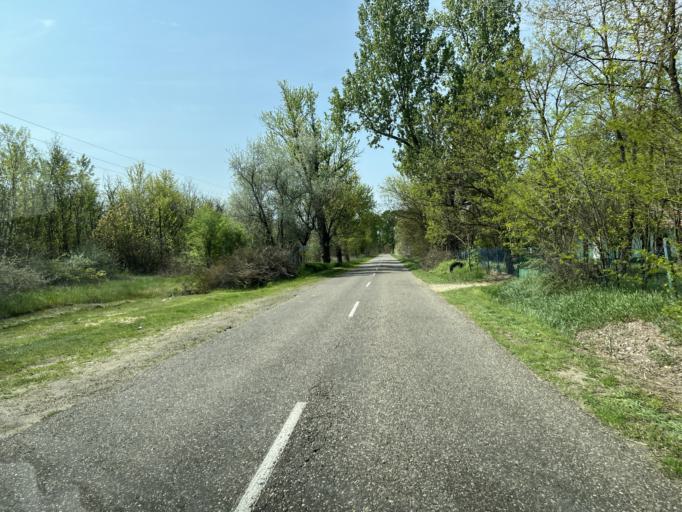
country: HU
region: Pest
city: Kocser
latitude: 47.0682
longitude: 19.8645
